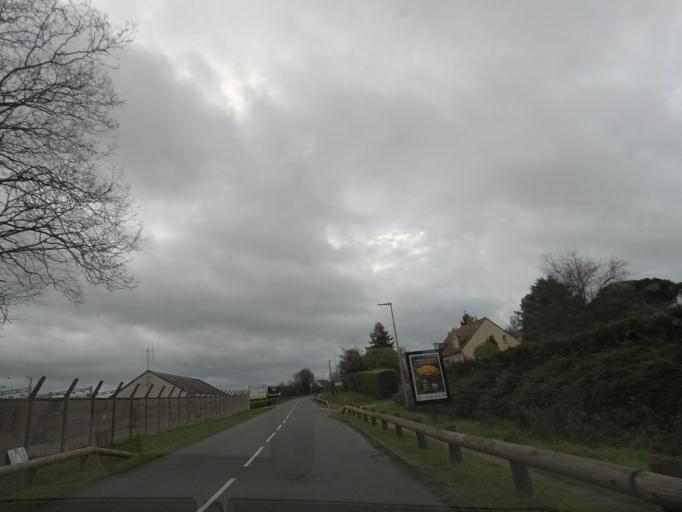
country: FR
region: Pays de la Loire
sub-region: Departement de la Sarthe
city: La Ferte-Bernard
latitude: 48.1979
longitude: 0.6381
